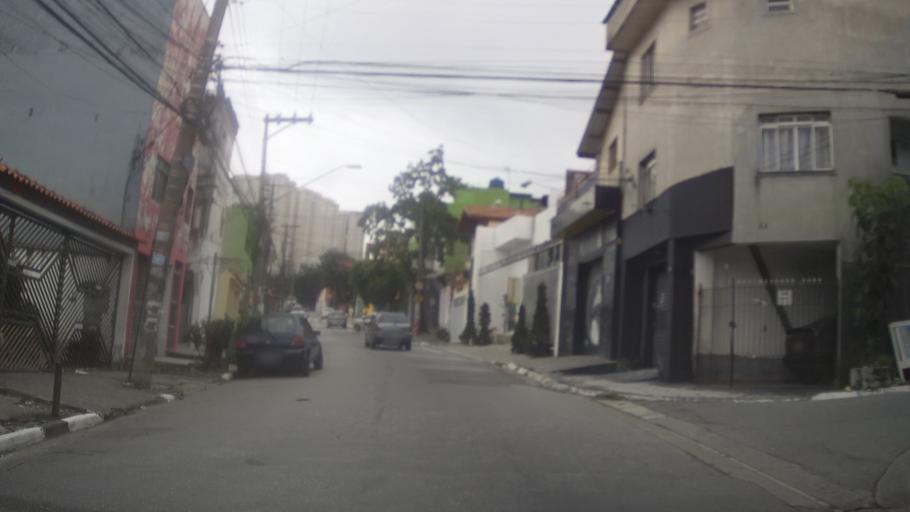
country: BR
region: Sao Paulo
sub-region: Guarulhos
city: Guarulhos
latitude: -23.4354
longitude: -46.5476
